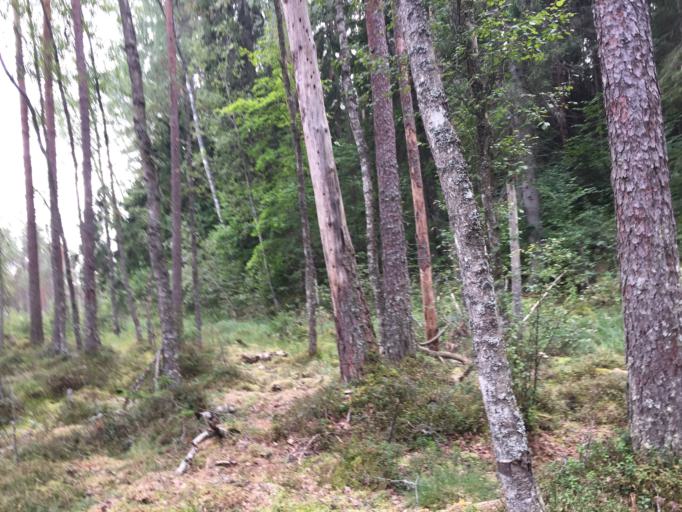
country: LV
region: Pargaujas
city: Stalbe
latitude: 57.3144
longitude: 25.0475
